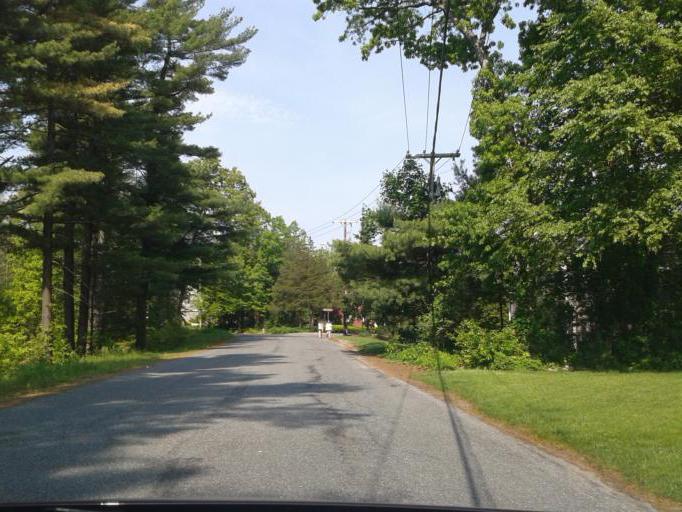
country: US
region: Massachusetts
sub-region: Worcester County
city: Westborough
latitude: 42.2426
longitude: -71.6093
